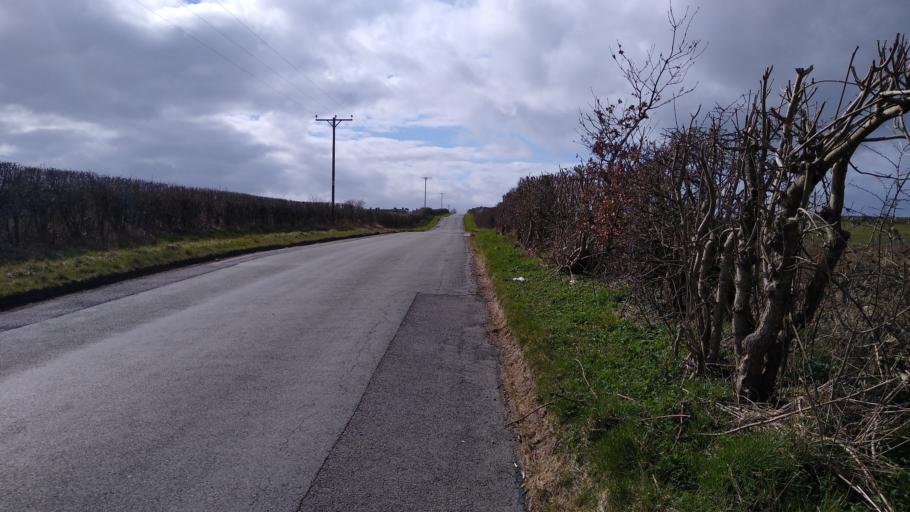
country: GB
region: England
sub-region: Cumbria
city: Dearham
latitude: 54.6897
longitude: -3.4575
